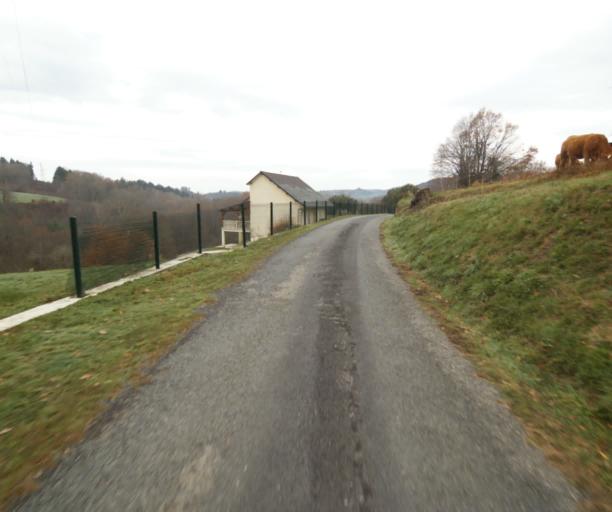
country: FR
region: Limousin
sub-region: Departement de la Correze
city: Chameyrat
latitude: 45.2356
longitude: 1.7390
